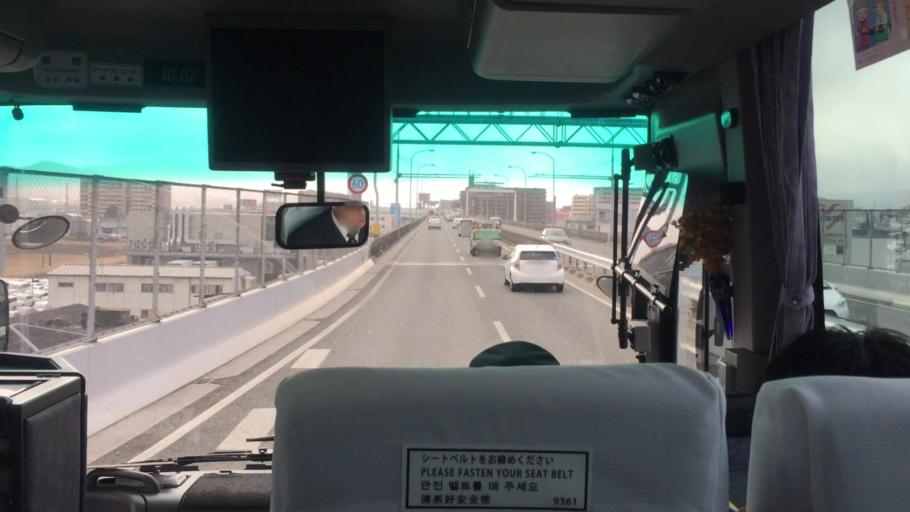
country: JP
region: Fukuoka
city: Fukuoka-shi
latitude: 33.5817
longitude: 130.4427
